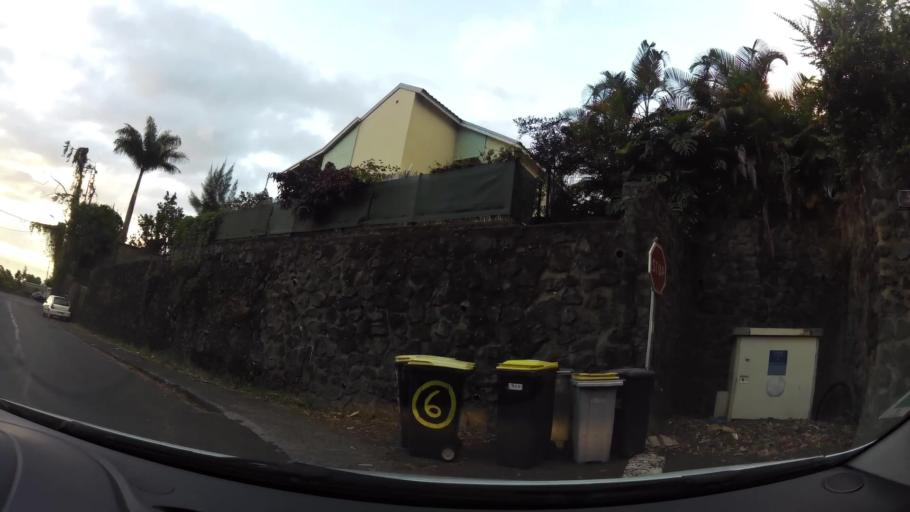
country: RE
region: Reunion
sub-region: Reunion
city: Saint-Denis
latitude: -20.9137
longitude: 55.4614
